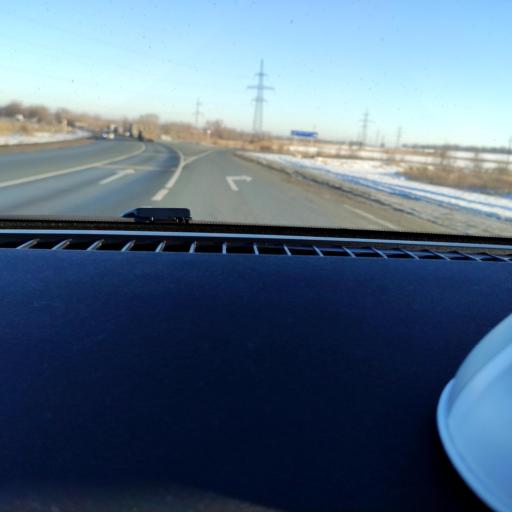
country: RU
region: Samara
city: Kinel'
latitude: 53.1487
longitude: 50.5094
